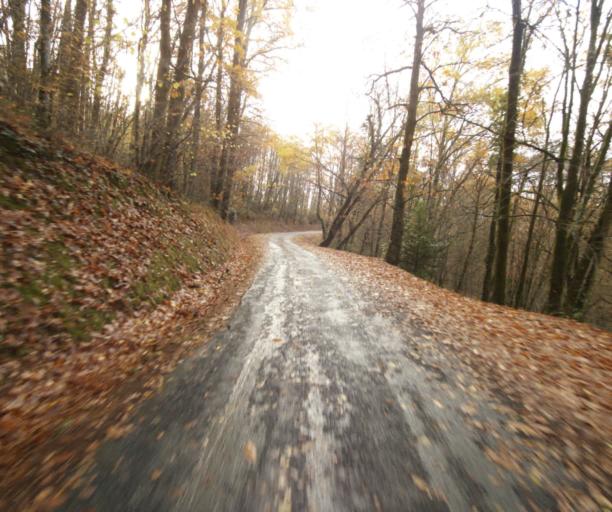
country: FR
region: Limousin
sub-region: Departement de la Correze
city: Sainte-Fereole
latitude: 45.2076
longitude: 1.6321
